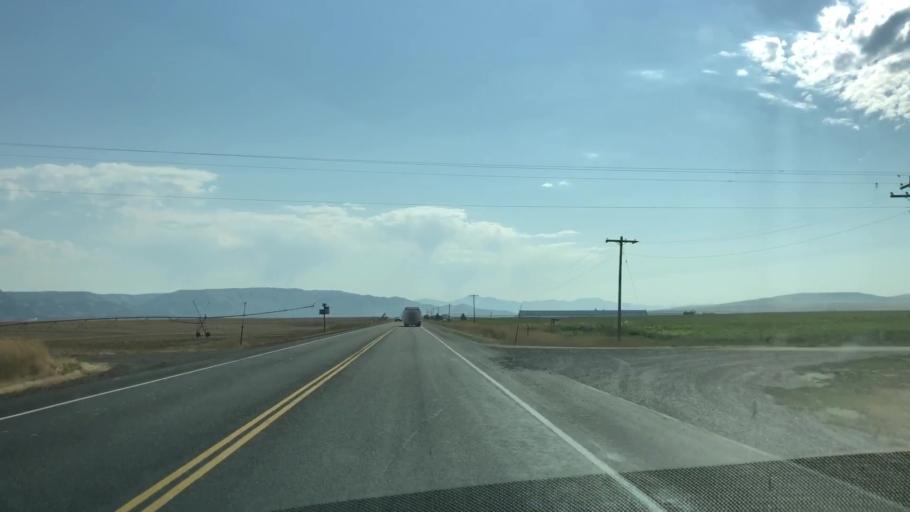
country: US
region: Idaho
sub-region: Jefferson County
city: Rigby
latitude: 43.6120
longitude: -111.7699
